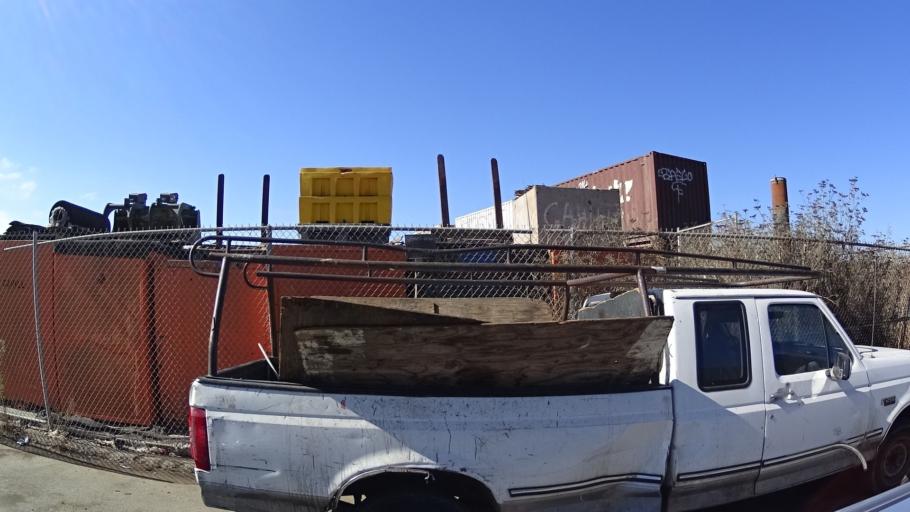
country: US
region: California
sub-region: San Francisco County
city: San Francisco
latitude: 37.7466
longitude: -122.3908
